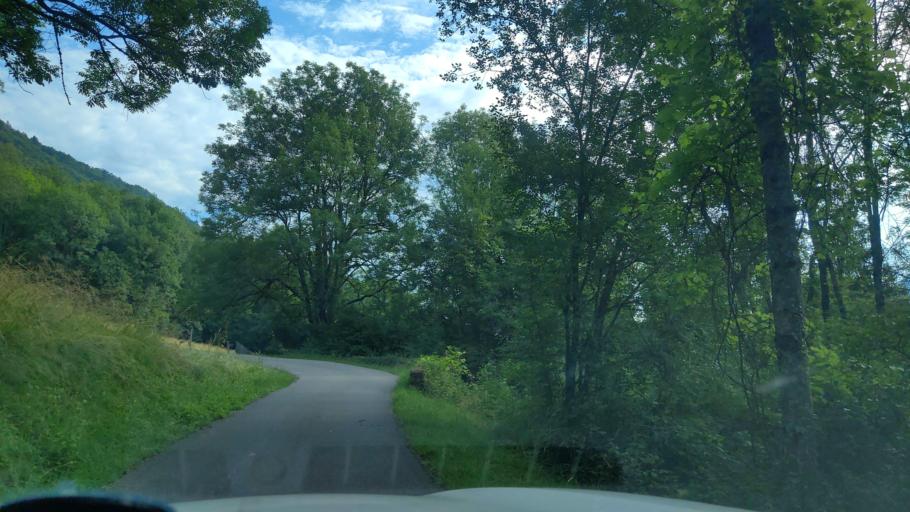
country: FR
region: Rhone-Alpes
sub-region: Departement de la Savoie
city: Coise-Saint-Jean-Pied-Gauthier
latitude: 45.4925
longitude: 6.1404
